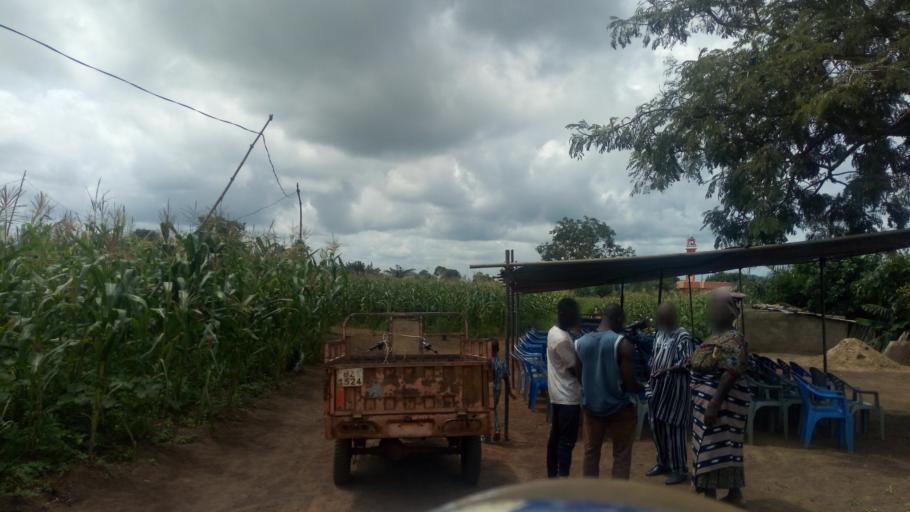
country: TG
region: Centrale
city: Sotouboua
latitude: 8.5536
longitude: 1.0034
